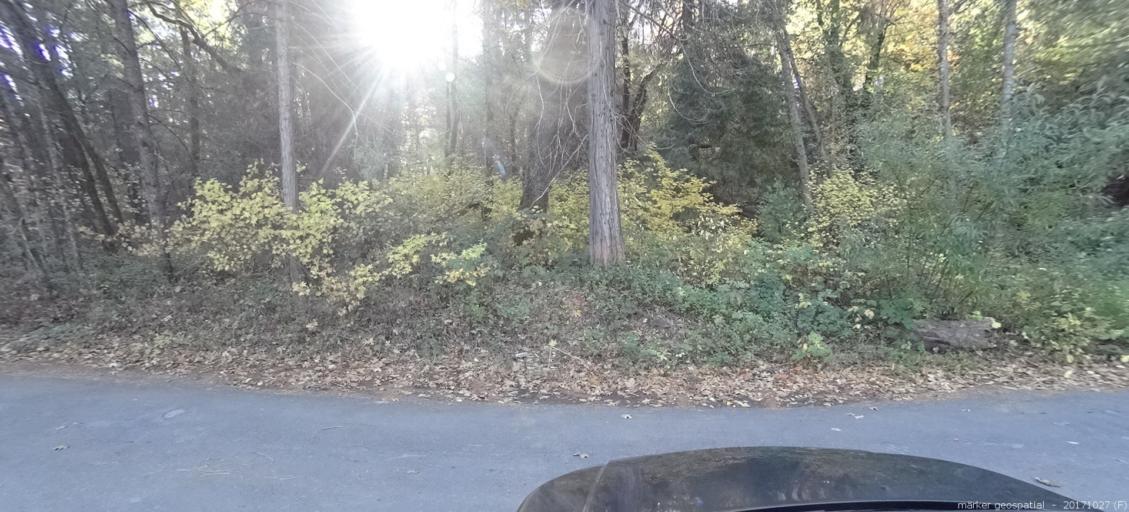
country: US
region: California
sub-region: Shasta County
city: Burney
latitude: 41.0210
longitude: -121.9170
